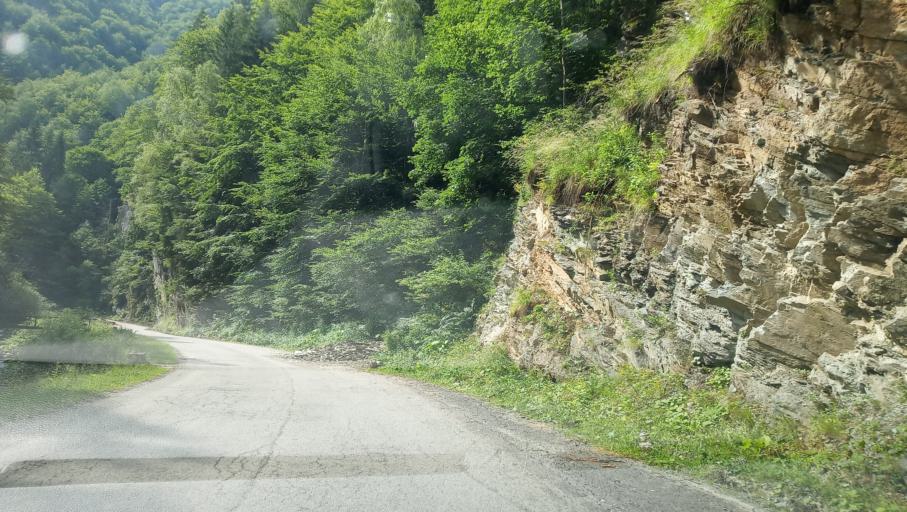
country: RO
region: Hunedoara
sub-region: Oras Petrila
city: Petrila
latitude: 45.4135
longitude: 23.4635
